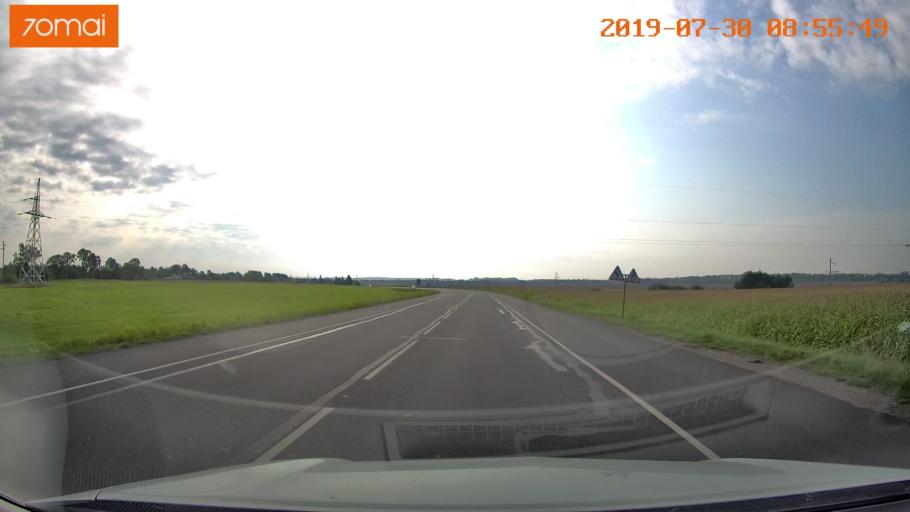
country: RU
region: Kaliningrad
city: Gusev
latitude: 54.5994
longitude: 22.0608
